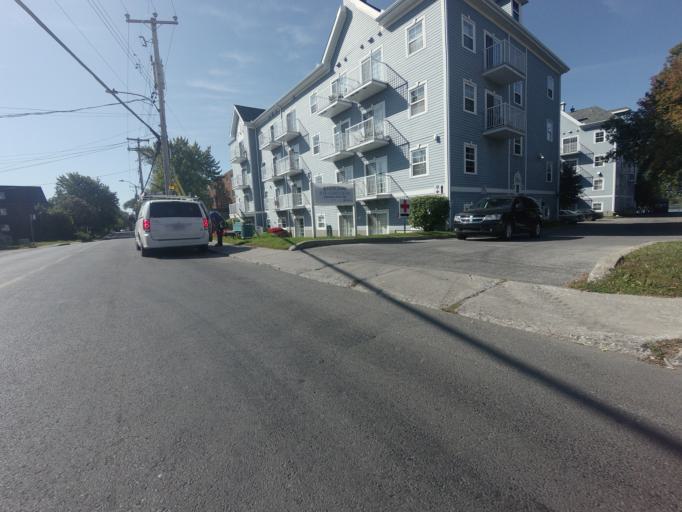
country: CA
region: Quebec
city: Kirkland
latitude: 45.4767
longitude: -73.8744
